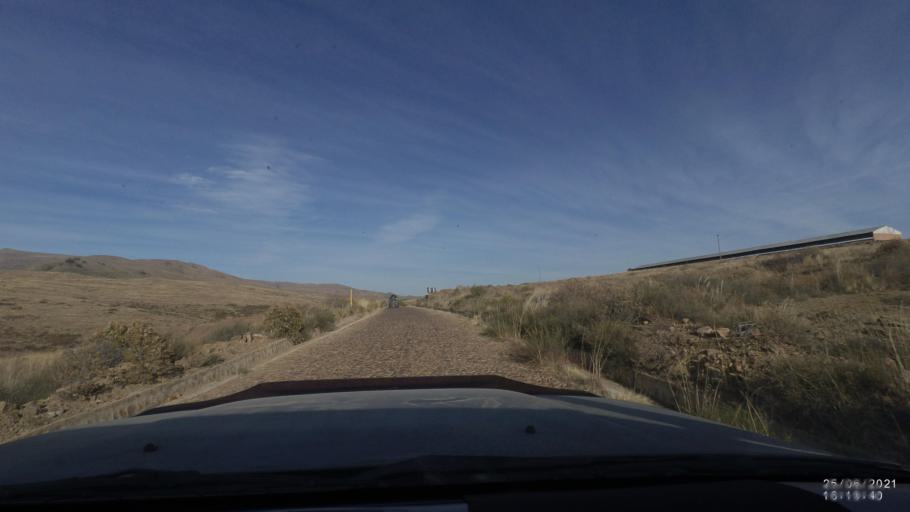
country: BO
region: Cochabamba
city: Cliza
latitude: -17.7418
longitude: -65.8449
